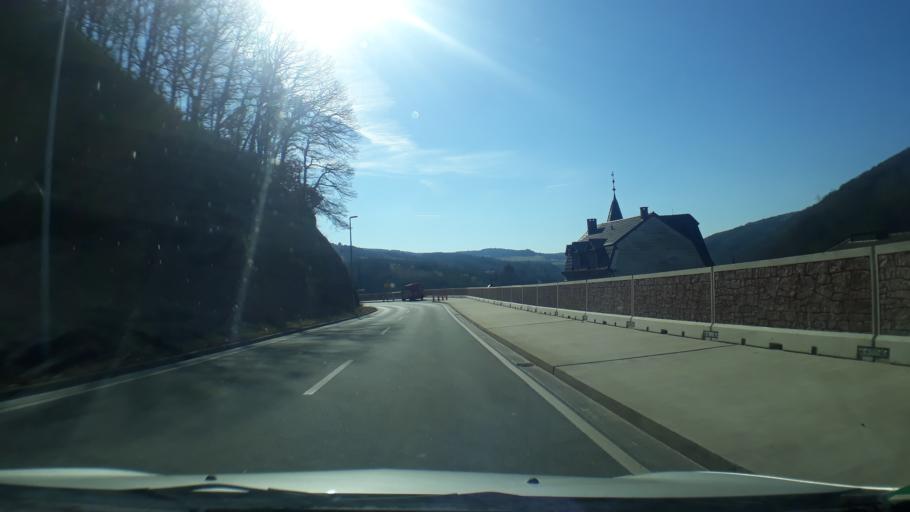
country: DE
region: North Rhine-Westphalia
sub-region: Regierungsbezirk Koln
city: Schleiden
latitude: 50.5743
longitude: 6.5002
